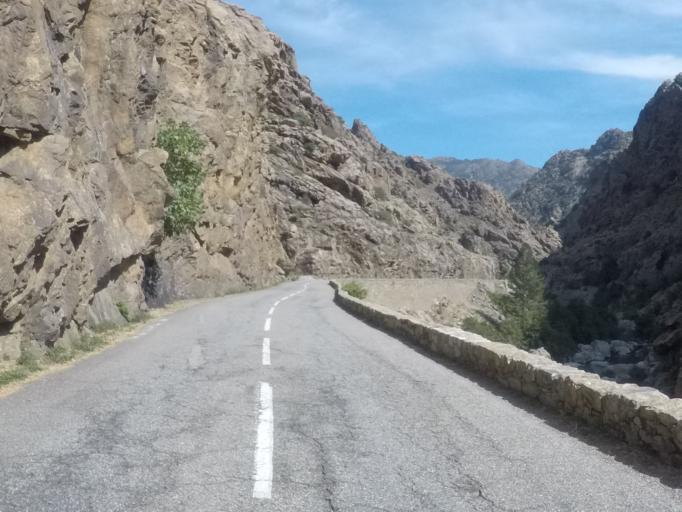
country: FR
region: Corsica
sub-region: Departement de la Haute-Corse
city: Corte
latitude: 42.3674
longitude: 9.0693
